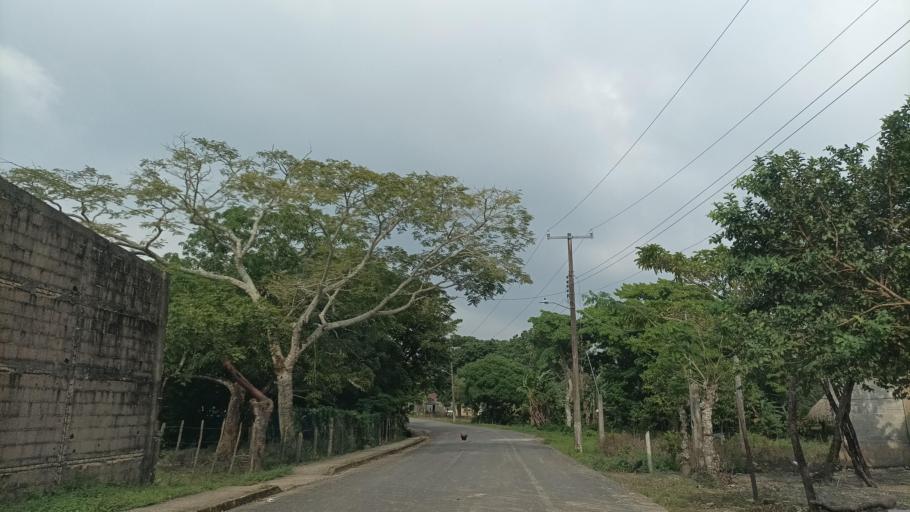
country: MX
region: Veracruz
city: Allende
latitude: 18.1241
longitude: -94.2834
